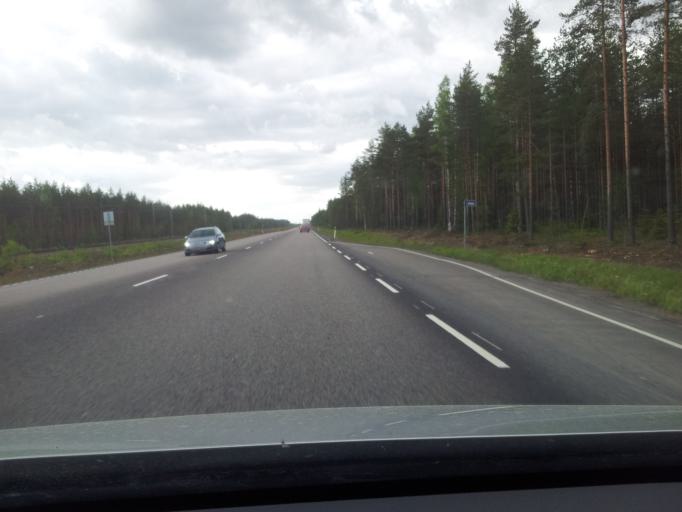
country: FI
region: South Karelia
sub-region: Lappeenranta
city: Taavetti
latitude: 60.9072
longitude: 27.2655
